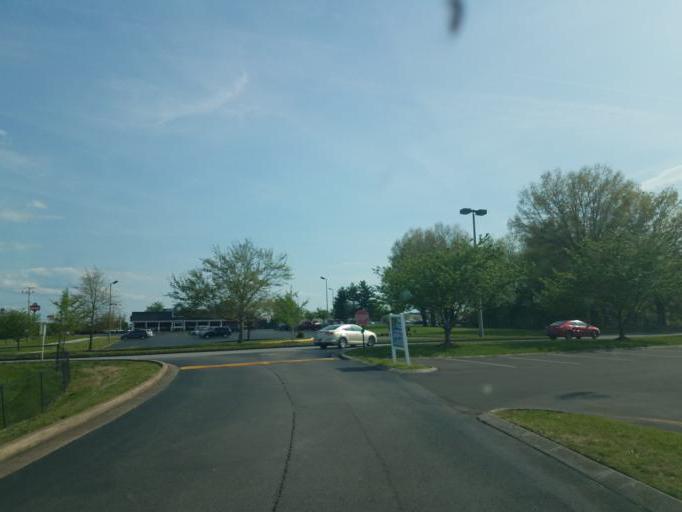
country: US
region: Kentucky
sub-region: Warren County
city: Bowling Green
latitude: 36.9526
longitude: -86.4267
